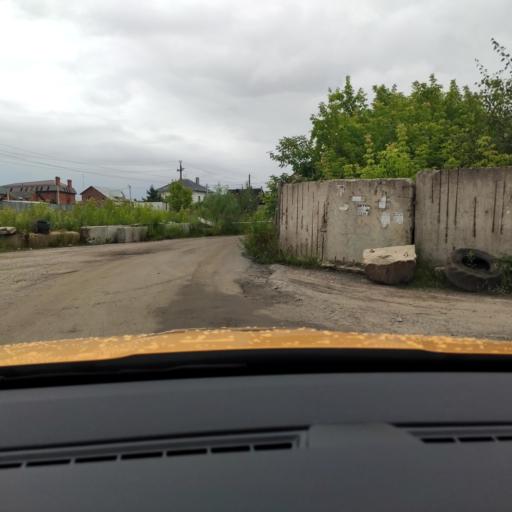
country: RU
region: Moscow
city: Vostochnyy
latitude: 55.8194
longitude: 37.8425
